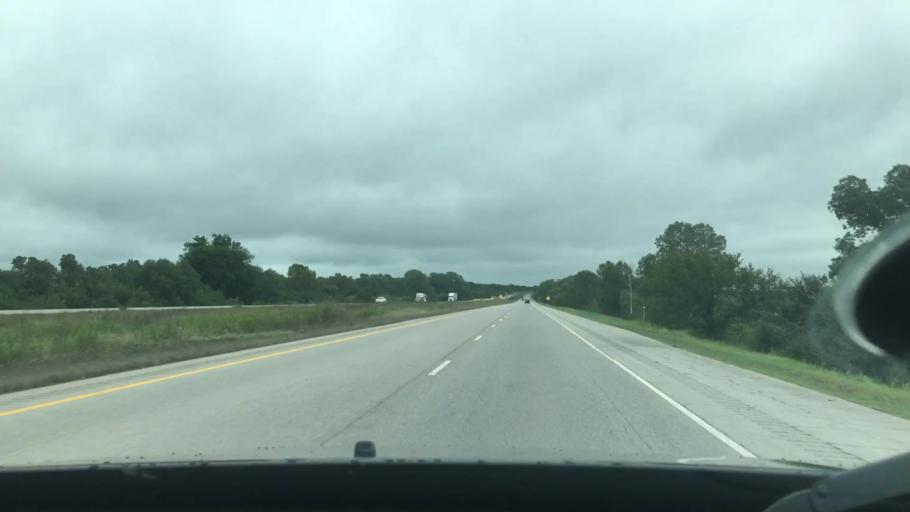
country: US
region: Oklahoma
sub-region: Okfuskee County
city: Okemah
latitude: 35.3905
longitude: -96.4088
